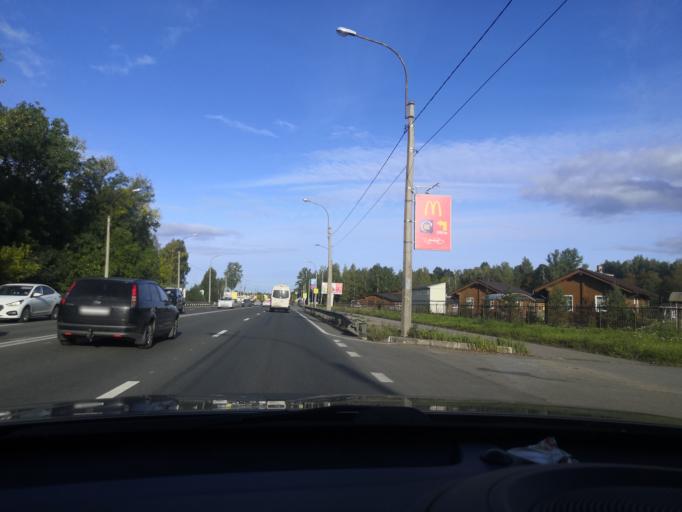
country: RU
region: St.-Petersburg
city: Pargolovo
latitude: 60.0743
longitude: 30.2790
